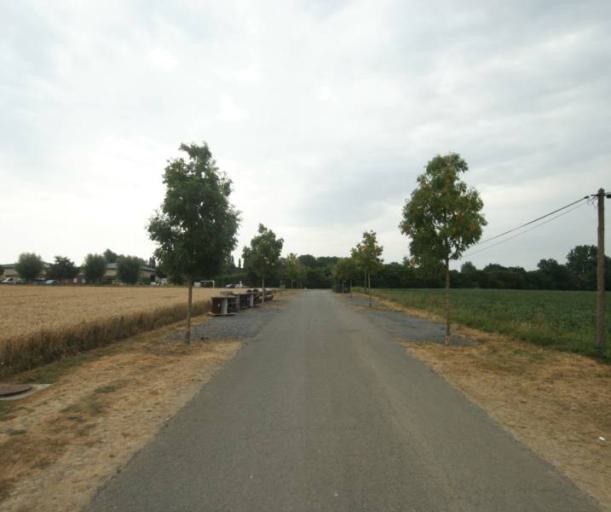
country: FR
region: Nord-Pas-de-Calais
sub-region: Departement du Nord
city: Bondues
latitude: 50.6934
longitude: 3.0803
